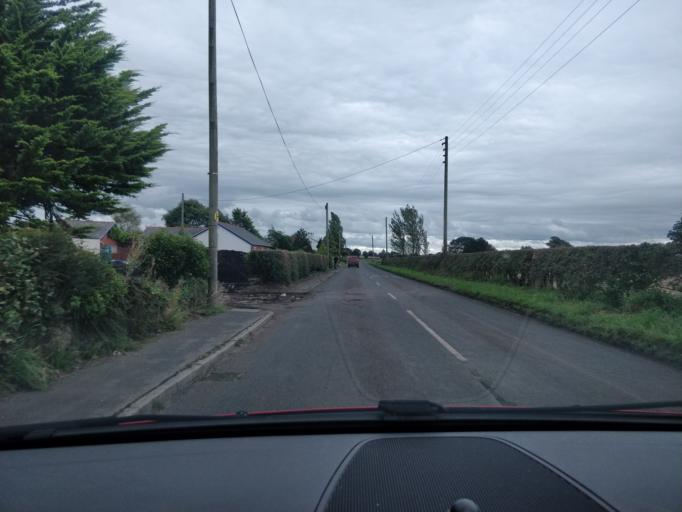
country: GB
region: England
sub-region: Lancashire
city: Ormskirk
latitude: 53.6183
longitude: -2.8493
